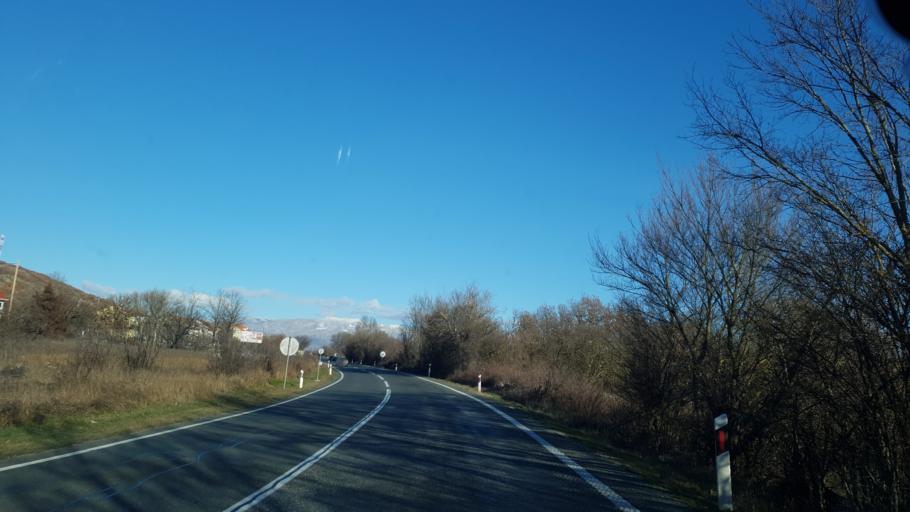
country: HR
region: Splitsko-Dalmatinska
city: Brnaze
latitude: 43.6453
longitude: 16.6260
